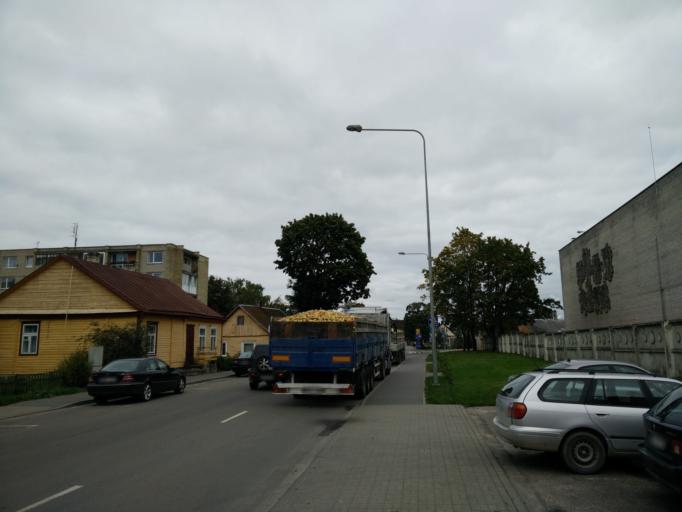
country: LT
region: Utenos apskritis
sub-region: Anyksciai
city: Anyksciai
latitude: 55.5246
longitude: 25.1089
